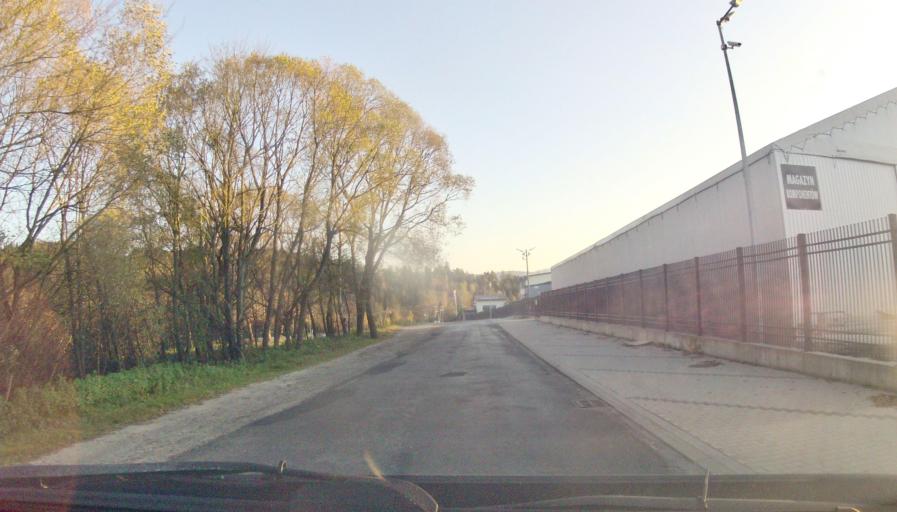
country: PL
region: Lesser Poland Voivodeship
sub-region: Powiat suski
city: Kukow
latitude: 49.7487
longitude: 19.4650
